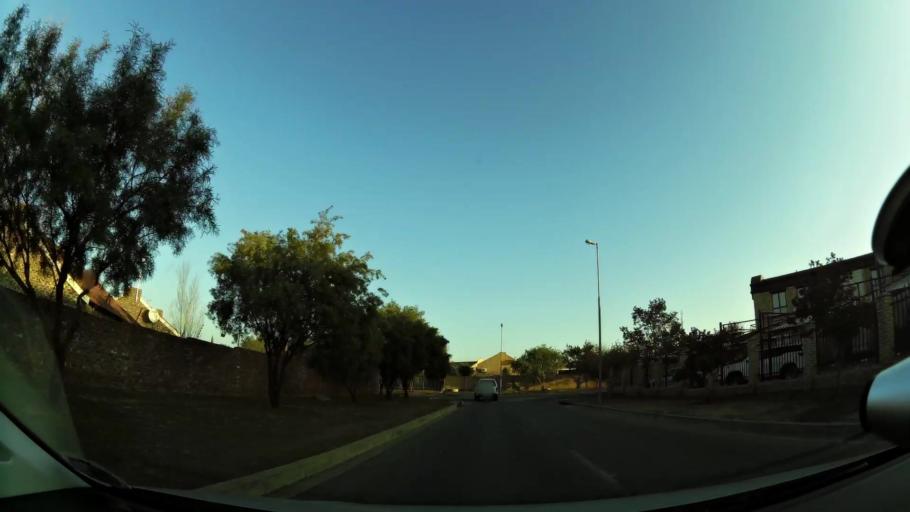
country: ZA
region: Orange Free State
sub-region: Mangaung Metropolitan Municipality
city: Bloemfontein
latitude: -29.0917
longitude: 26.1666
